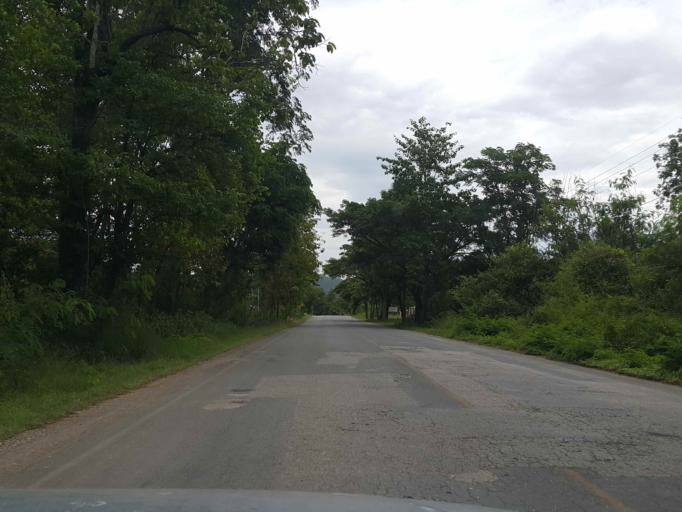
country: TH
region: Lampang
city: Thoen
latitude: 17.5900
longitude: 99.3311
